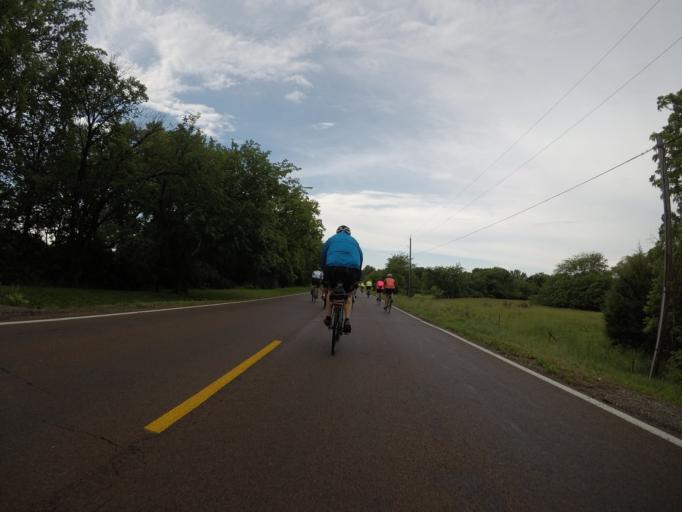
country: US
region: Kansas
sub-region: Shawnee County
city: Topeka
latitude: 38.9735
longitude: -95.7145
